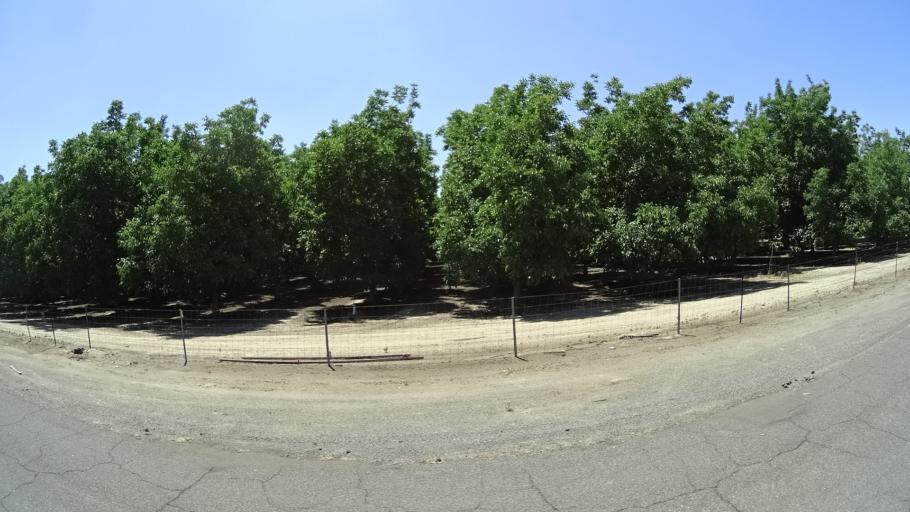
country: US
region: California
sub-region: Fresno County
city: Kingsburg
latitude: 36.4814
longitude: -119.5729
